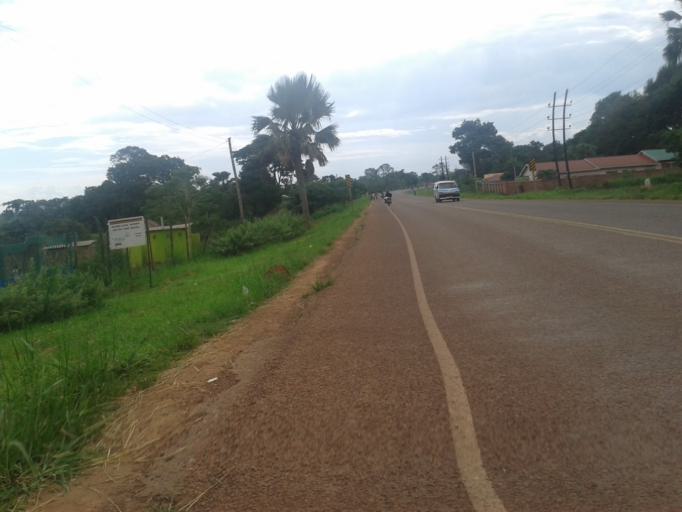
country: UG
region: Northern Region
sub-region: Gulu District
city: Gulu
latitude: 2.7619
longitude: 32.2771
